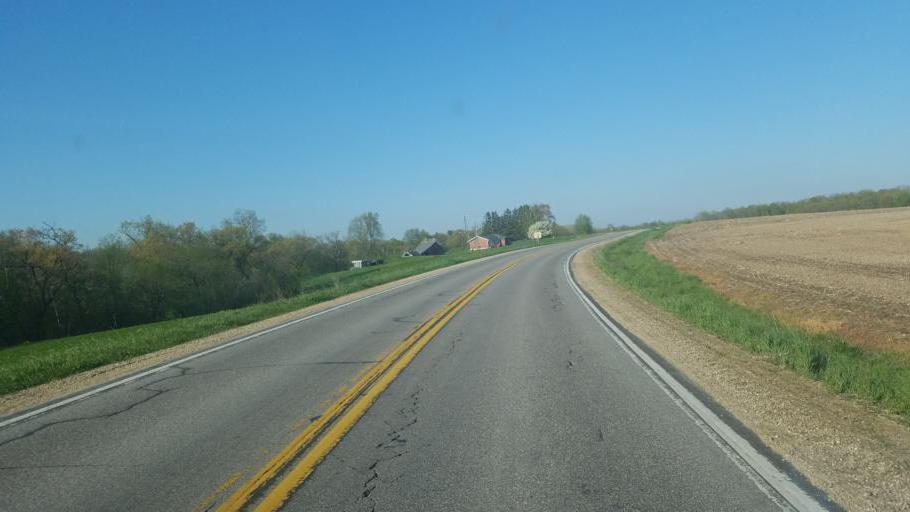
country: US
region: Wisconsin
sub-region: Vernon County
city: Hillsboro
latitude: 43.6170
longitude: -90.4533
